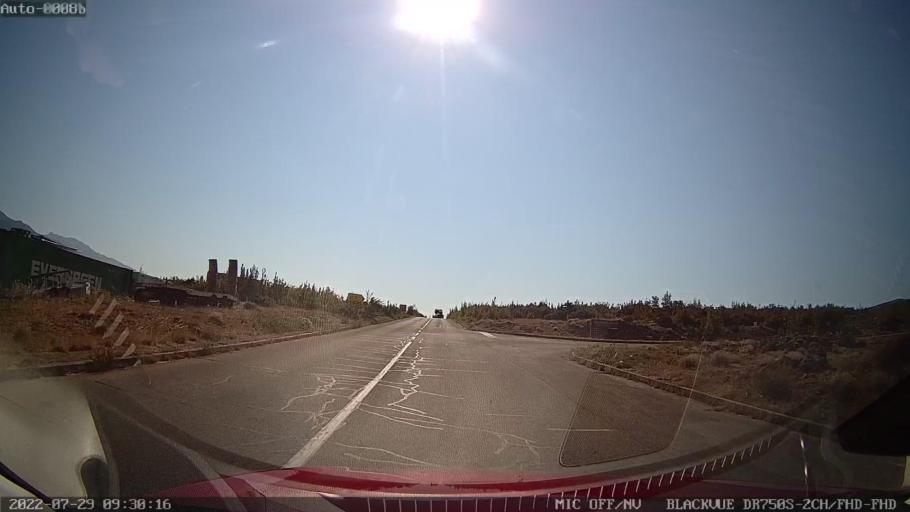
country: HR
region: Zadarska
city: Obrovac
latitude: 44.1941
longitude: 15.6840
